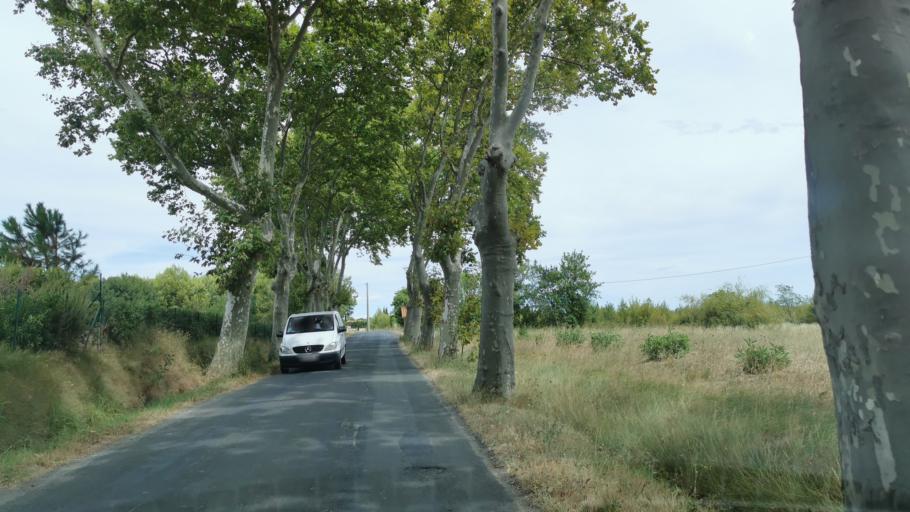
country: FR
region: Languedoc-Roussillon
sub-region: Departement de l'Aude
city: Ginestas
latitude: 43.2711
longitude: 2.8808
